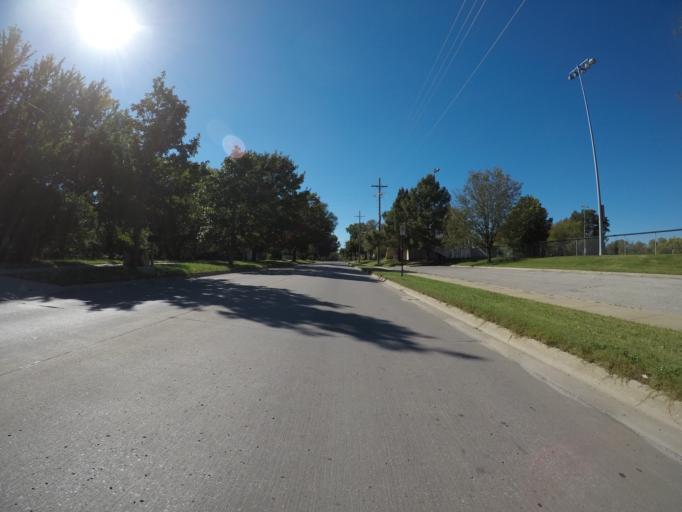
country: US
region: Kansas
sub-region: Douglas County
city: Lawrence
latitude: 38.9638
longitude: -95.2266
